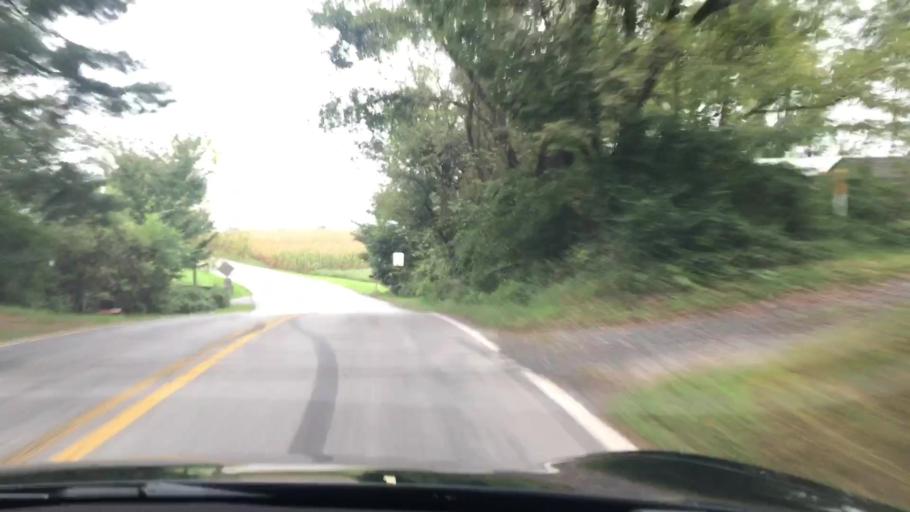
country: US
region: Pennsylvania
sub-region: York County
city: Weigelstown
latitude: 39.9512
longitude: -76.8602
